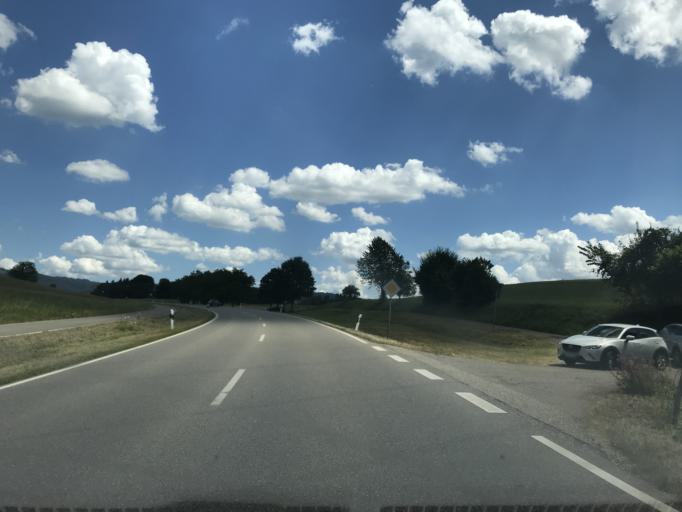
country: DE
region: Baden-Wuerttemberg
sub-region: Freiburg Region
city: Schopfheim
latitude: 47.6473
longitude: 7.8542
